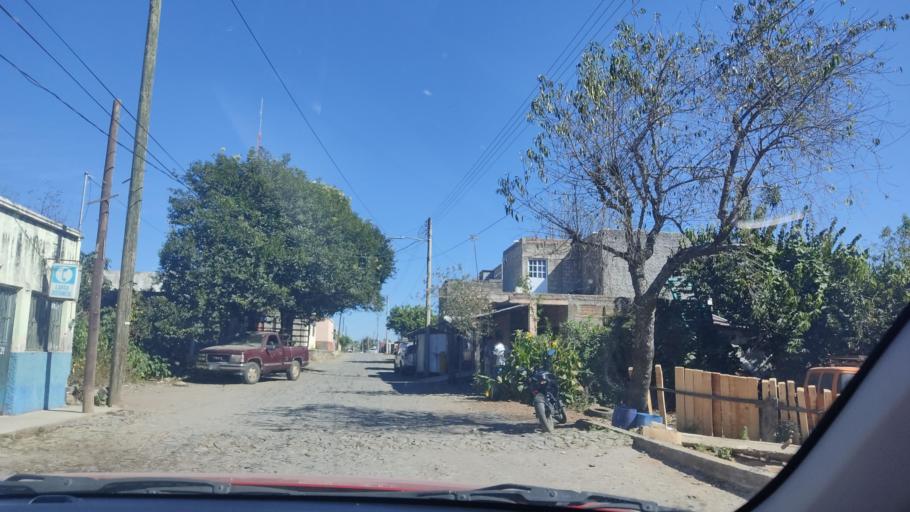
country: MX
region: Nayarit
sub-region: Jala
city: Rosa Blanca
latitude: 21.1073
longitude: -104.3541
